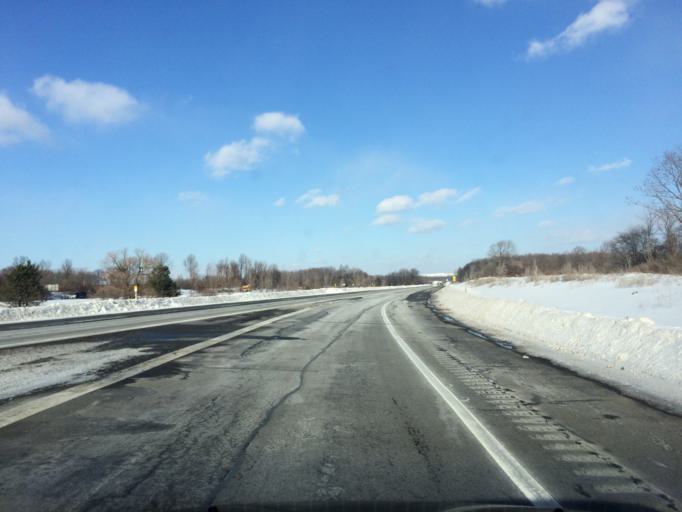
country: US
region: New York
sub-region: Genesee County
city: Bergen
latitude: 43.0381
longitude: -77.9603
